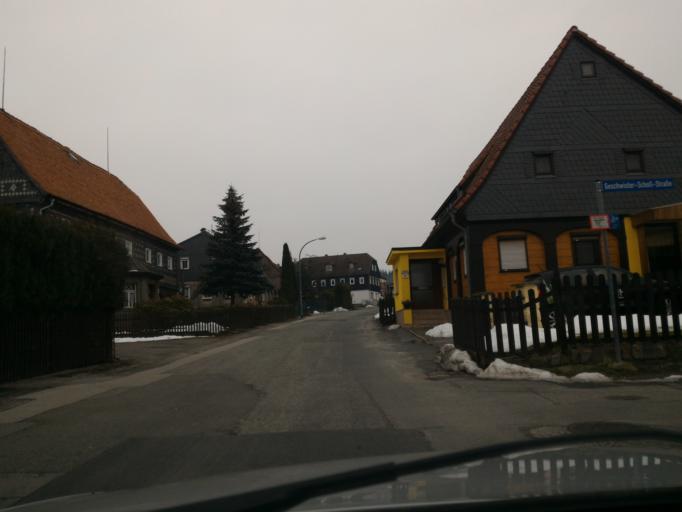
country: DE
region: Saxony
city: Neugersdorf
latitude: 50.9736
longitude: 14.6098
